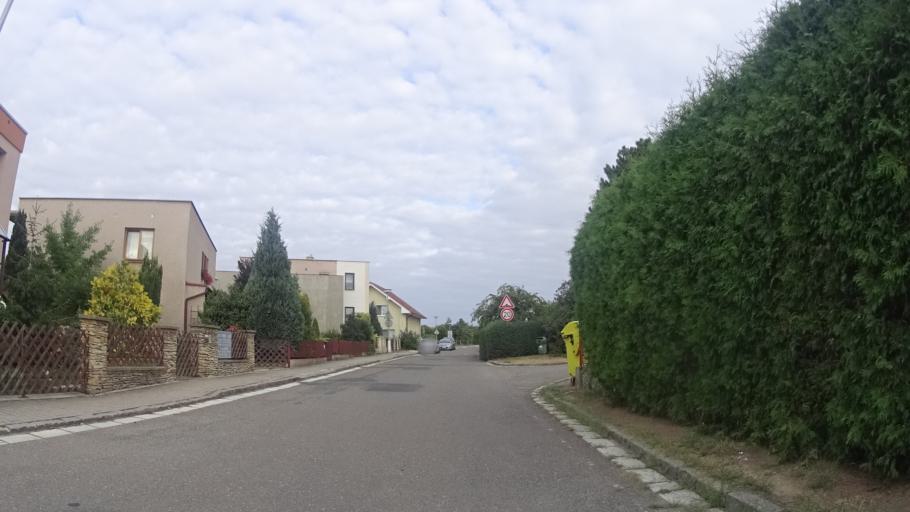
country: CZ
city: Stezery
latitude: 50.2117
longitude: 15.7483
